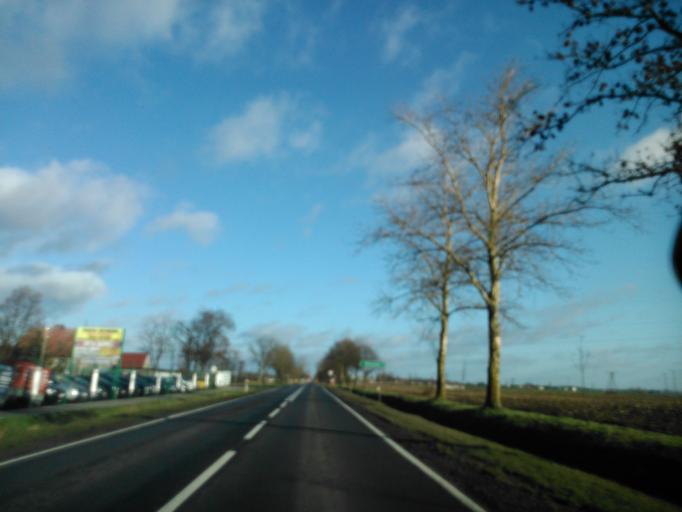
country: PL
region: Kujawsko-Pomorskie
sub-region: Powiat inowroclawski
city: Wierzchoslawice
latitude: 52.8795
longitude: 18.3827
